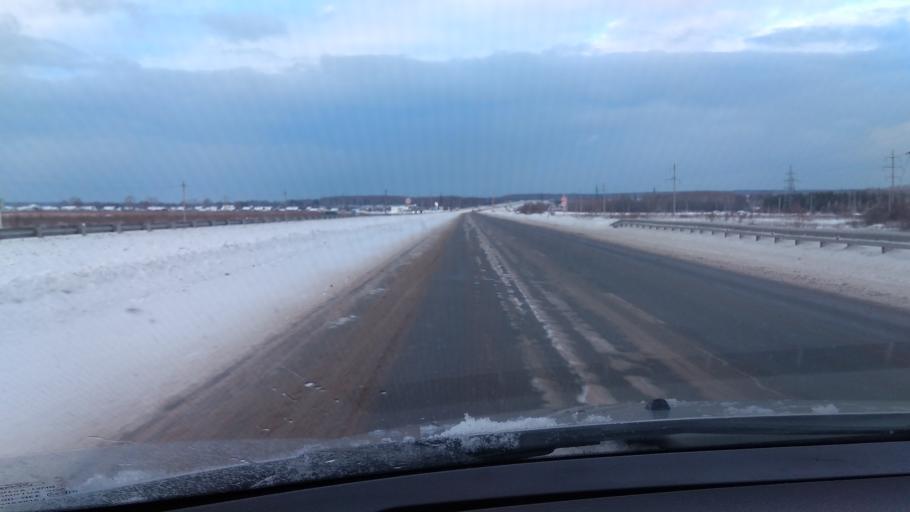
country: RU
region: Sverdlovsk
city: Tsementnyy
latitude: 57.4915
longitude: 60.1777
